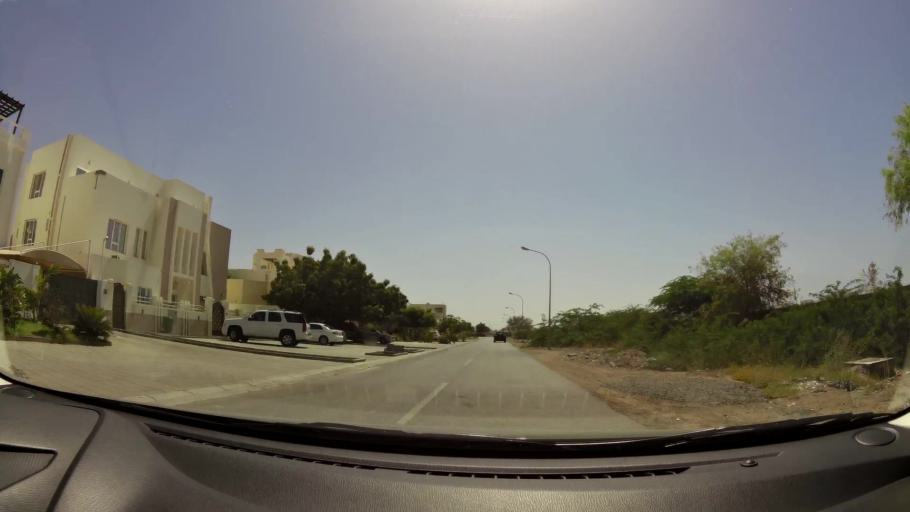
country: OM
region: Muhafazat Masqat
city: Bawshar
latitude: 23.6006
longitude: 58.3549
